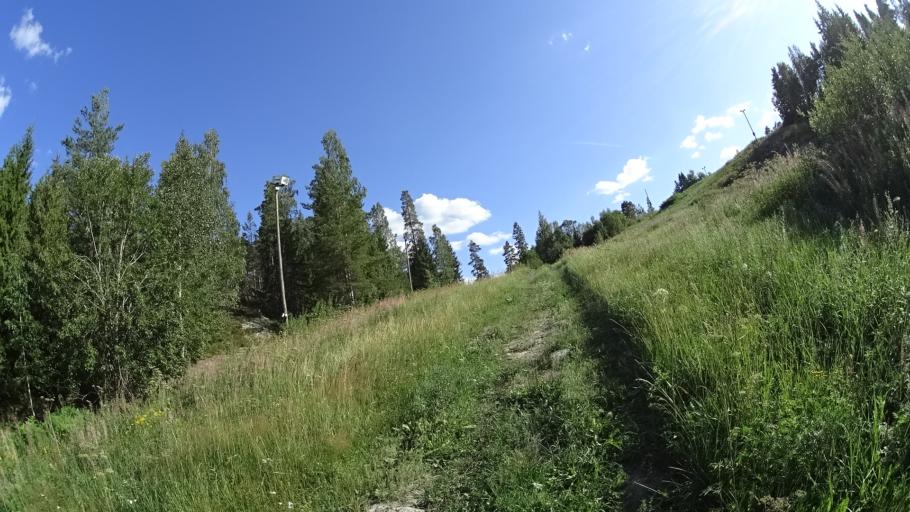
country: FI
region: Uusimaa
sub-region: Helsinki
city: Vihti
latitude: 60.3773
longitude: 24.3707
